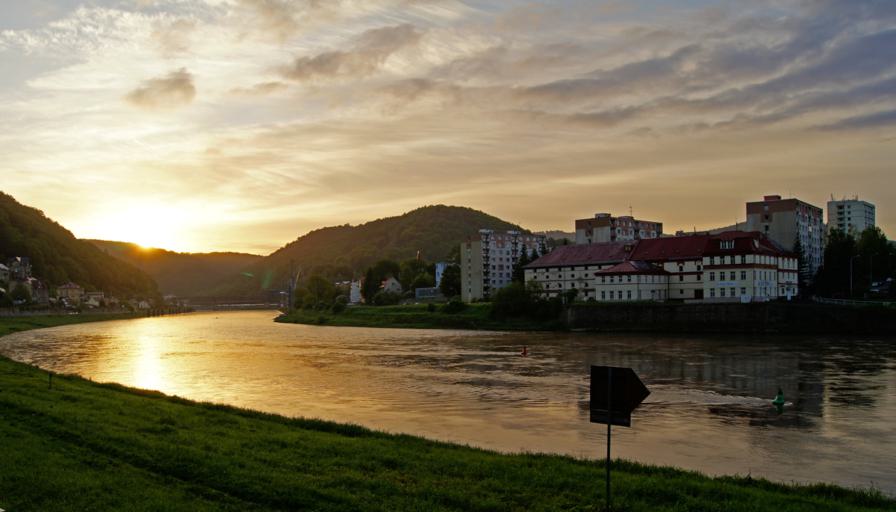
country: CZ
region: Ustecky
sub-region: Okres Decin
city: Decin
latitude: 50.7827
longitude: 14.2076
